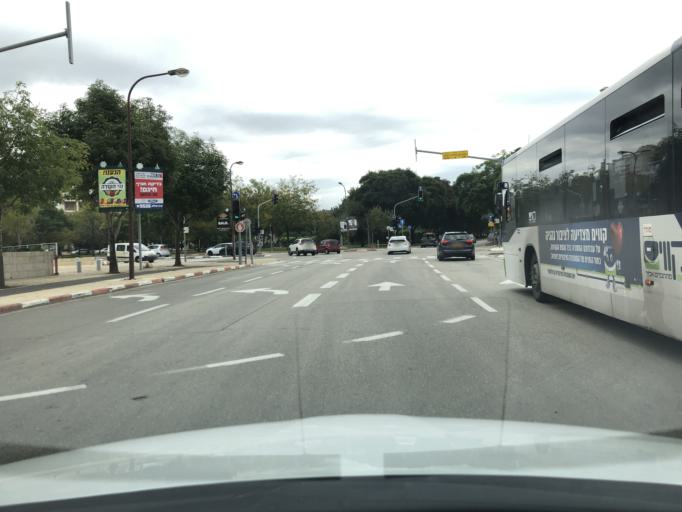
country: IL
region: Central District
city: Modiin
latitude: 31.8987
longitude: 35.0085
